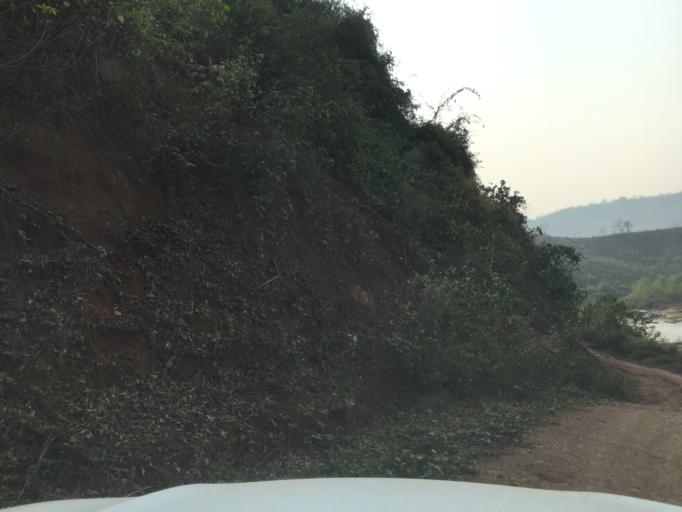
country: LA
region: Xiangkhoang
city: Phonsavan
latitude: 19.8265
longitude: 102.9884
